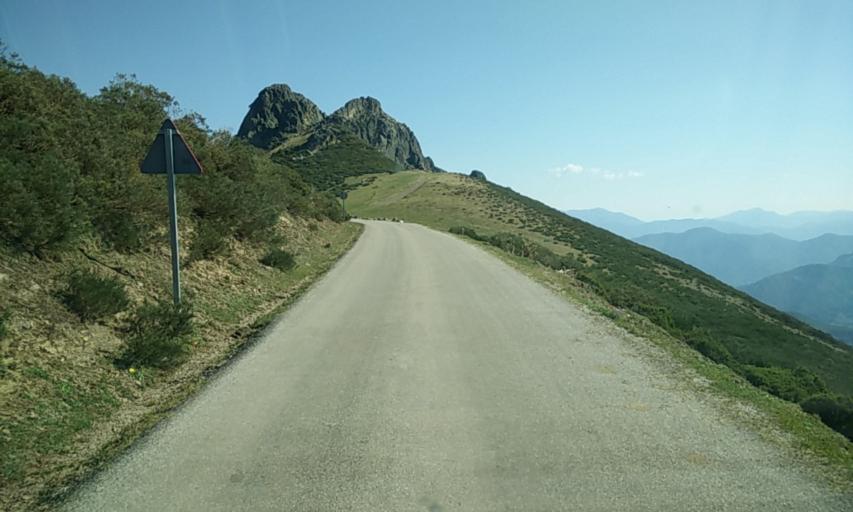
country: ES
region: Cantabria
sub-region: Provincia de Cantabria
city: Camaleno
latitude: 43.0756
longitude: -4.7510
